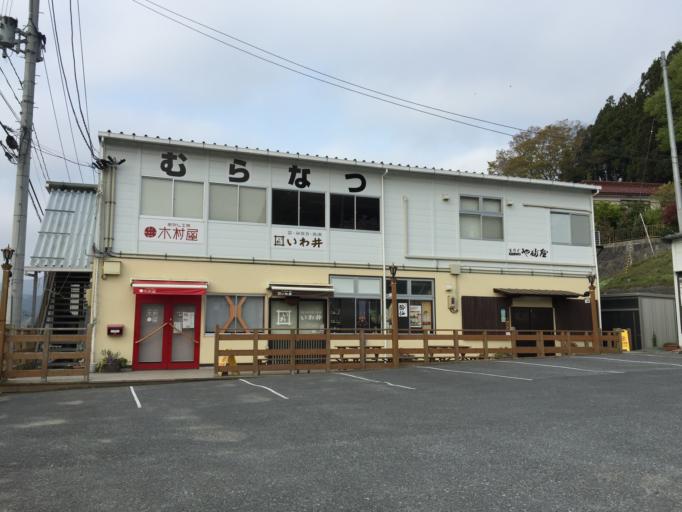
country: JP
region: Iwate
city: Ofunato
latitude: 39.0230
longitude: 141.6233
